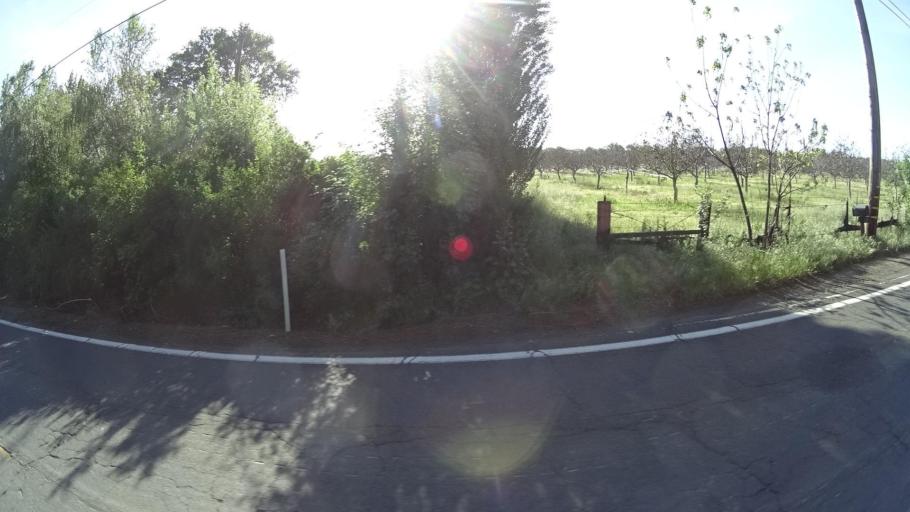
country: US
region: California
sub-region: Lake County
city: North Lakeport
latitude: 39.0771
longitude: -122.9498
